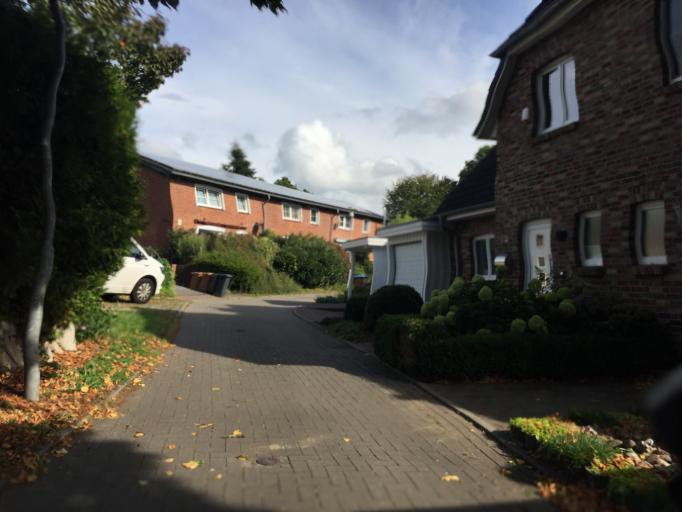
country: DE
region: Schleswig-Holstein
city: Itzehoe
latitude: 53.9278
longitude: 9.4997
